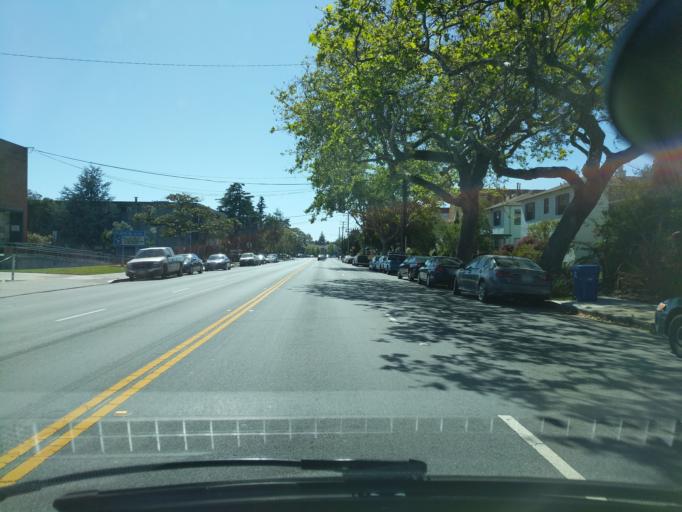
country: US
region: California
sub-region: Alameda County
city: Oakland
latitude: 37.7716
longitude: -122.2835
